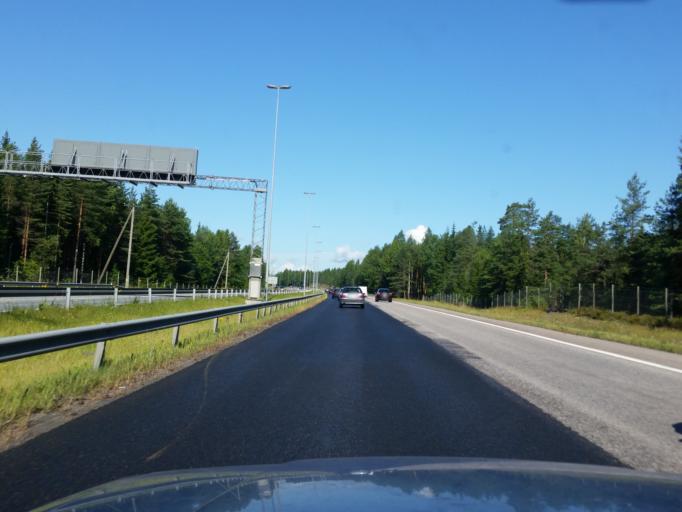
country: FI
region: Uusimaa
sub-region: Helsinki
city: Espoo
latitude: 60.2524
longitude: 24.5290
